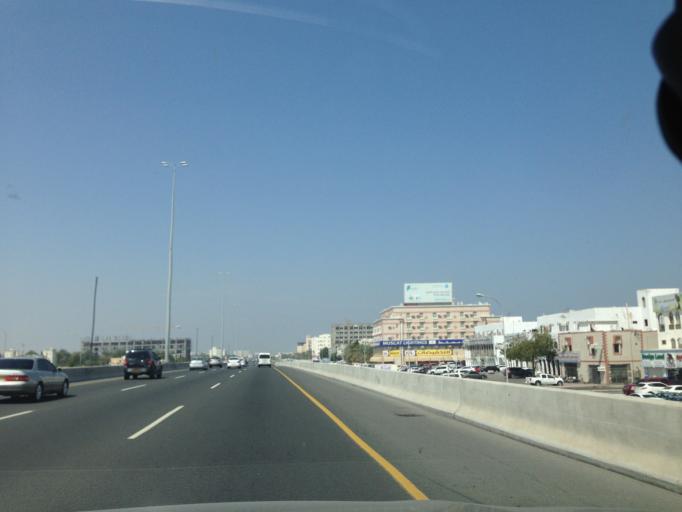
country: OM
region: Muhafazat Masqat
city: As Sib al Jadidah
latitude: 23.6353
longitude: 58.2291
